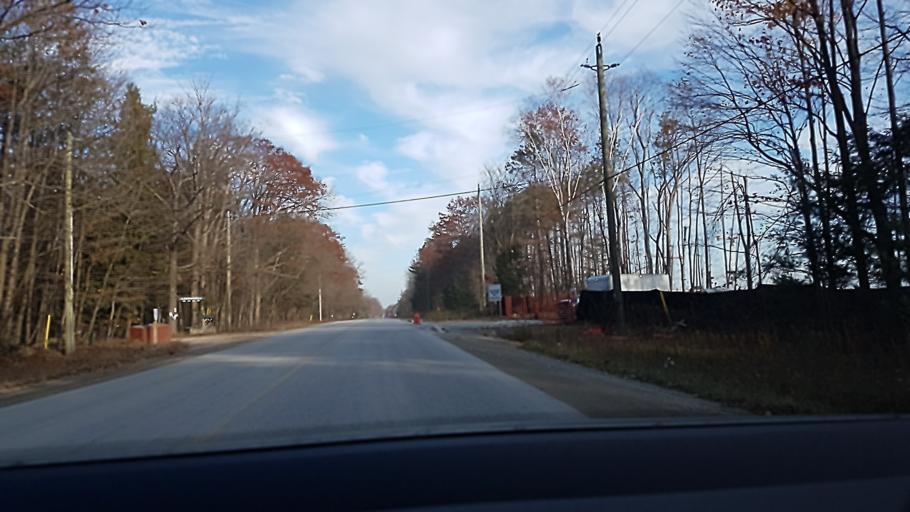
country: CA
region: Ontario
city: Barrie
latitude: 44.3943
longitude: -79.5399
